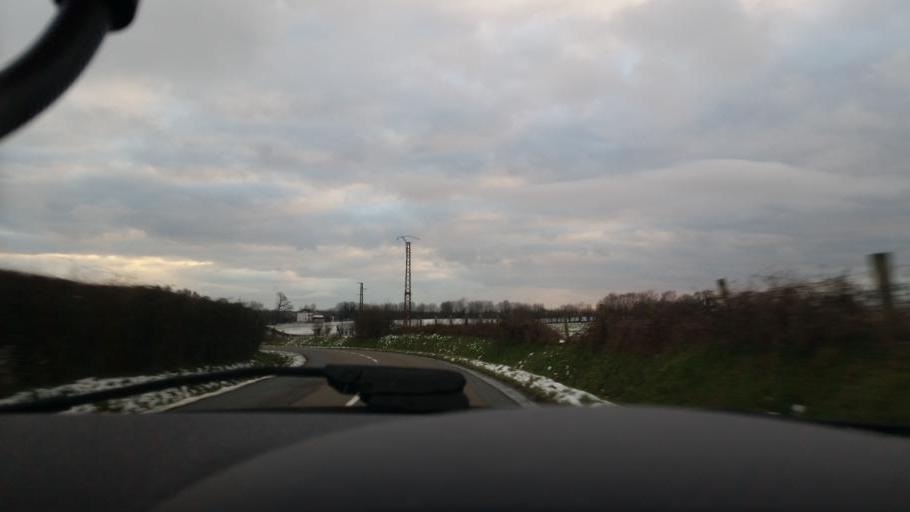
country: FR
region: Nord-Pas-de-Calais
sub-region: Departement du Nord
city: Marpent
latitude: 50.2474
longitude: 4.0984
